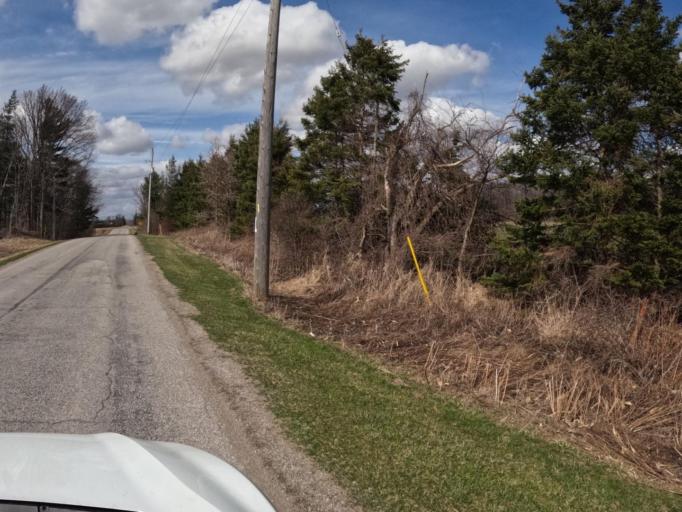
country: CA
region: Ontario
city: Norfolk County
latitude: 42.8725
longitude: -80.1946
